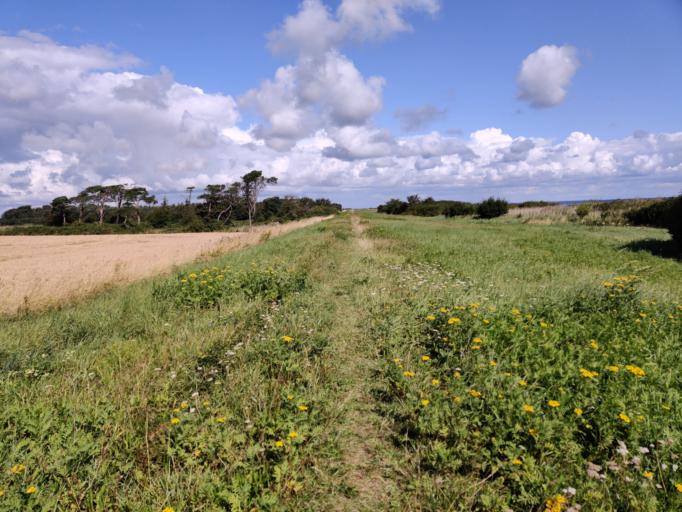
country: DK
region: Zealand
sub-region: Guldborgsund Kommune
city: Nykobing Falster
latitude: 54.5761
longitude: 11.9725
